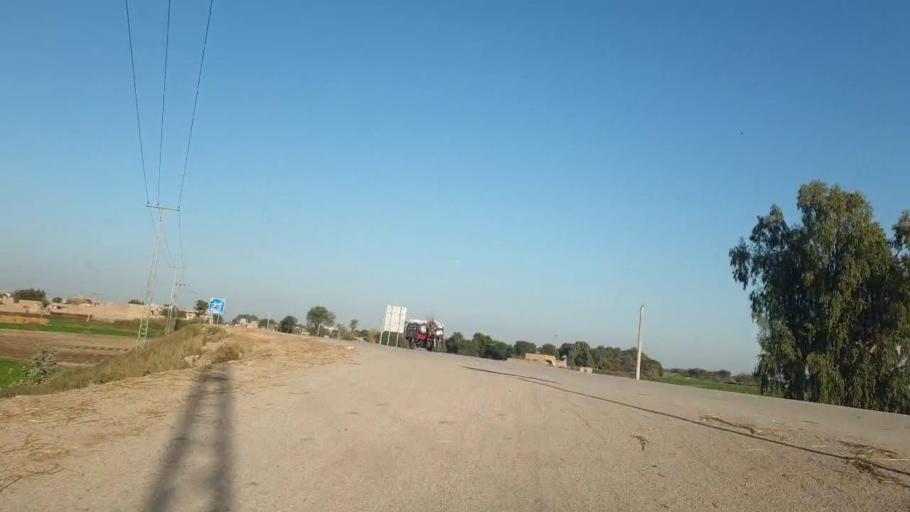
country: PK
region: Sindh
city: Dokri
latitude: 27.3727
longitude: 68.1249
